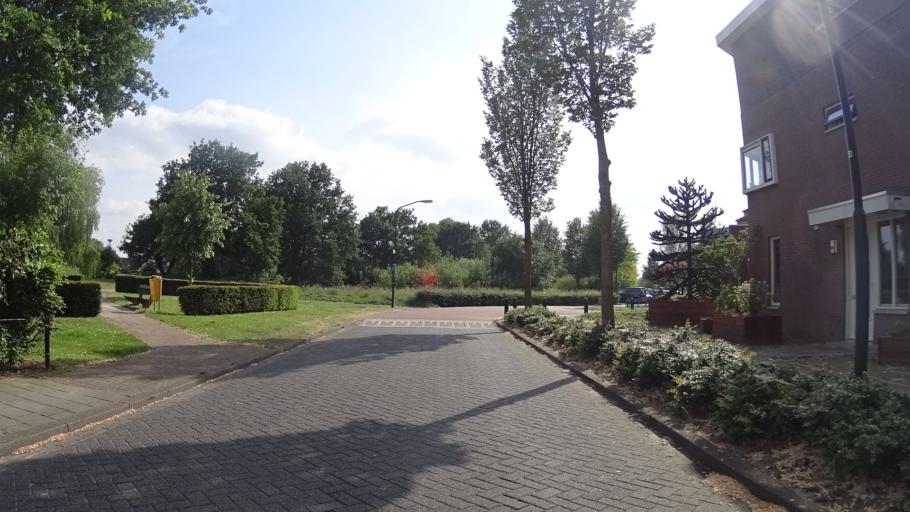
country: NL
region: North Brabant
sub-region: Gemeente Veghel
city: Veghel
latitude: 51.6309
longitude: 5.5602
